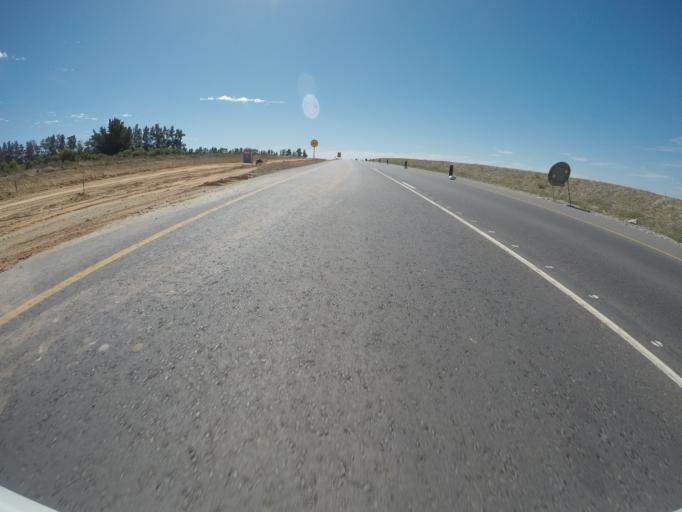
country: ZA
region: Western Cape
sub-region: West Coast District Municipality
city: Malmesbury
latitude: -33.5029
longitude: 18.6627
